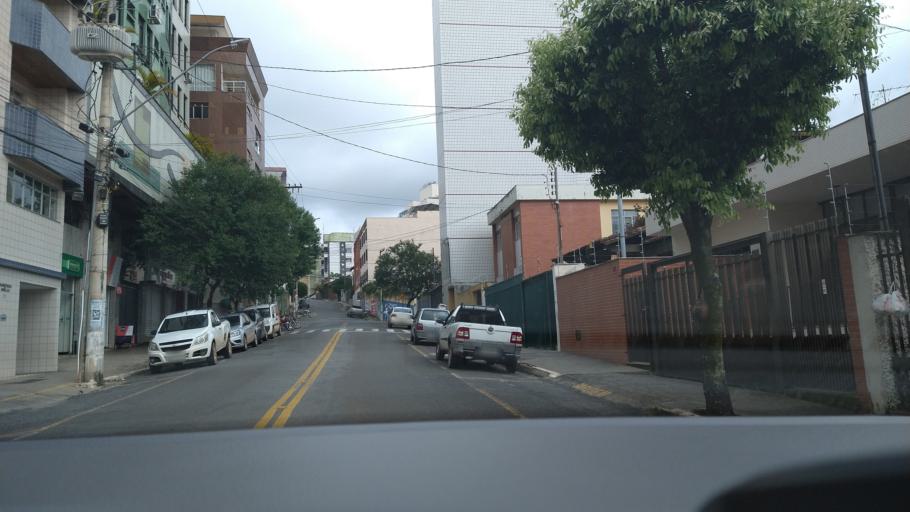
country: BR
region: Minas Gerais
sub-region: Vicosa
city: Vicosa
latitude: -20.7571
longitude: -42.8807
